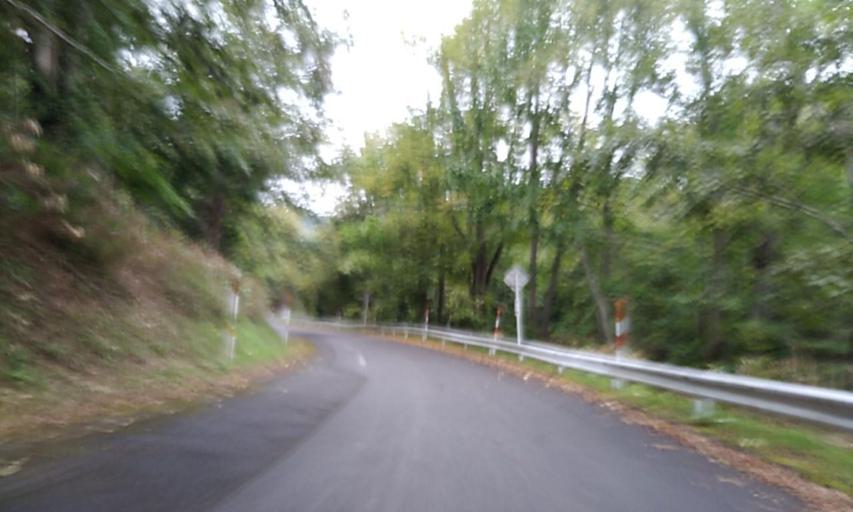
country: JP
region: Hokkaido
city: Bihoro
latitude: 43.5660
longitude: 144.1936
